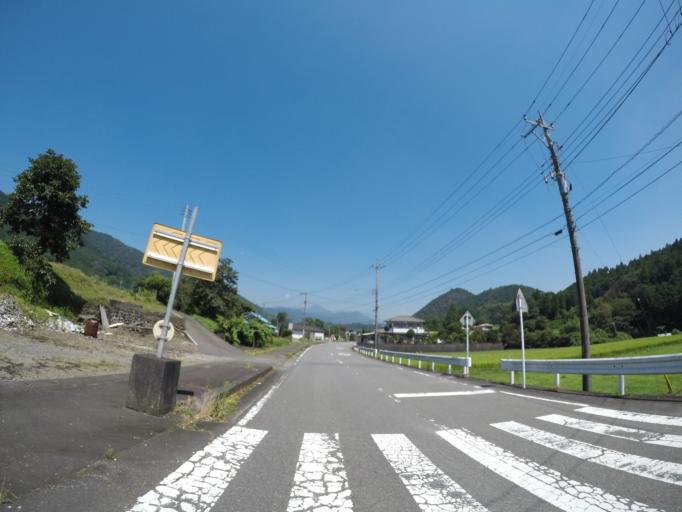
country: JP
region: Shizuoka
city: Fujinomiya
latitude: 35.2186
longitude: 138.5667
